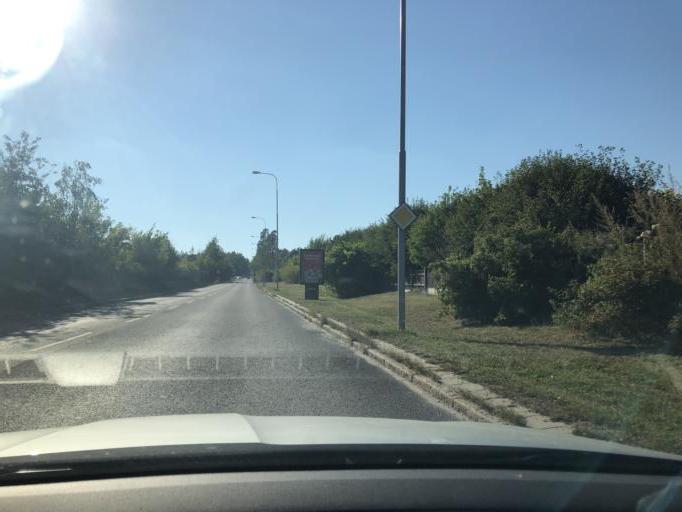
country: SE
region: Stockholm
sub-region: Sodertalje Kommun
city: Soedertaelje
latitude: 59.1824
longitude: 17.6153
